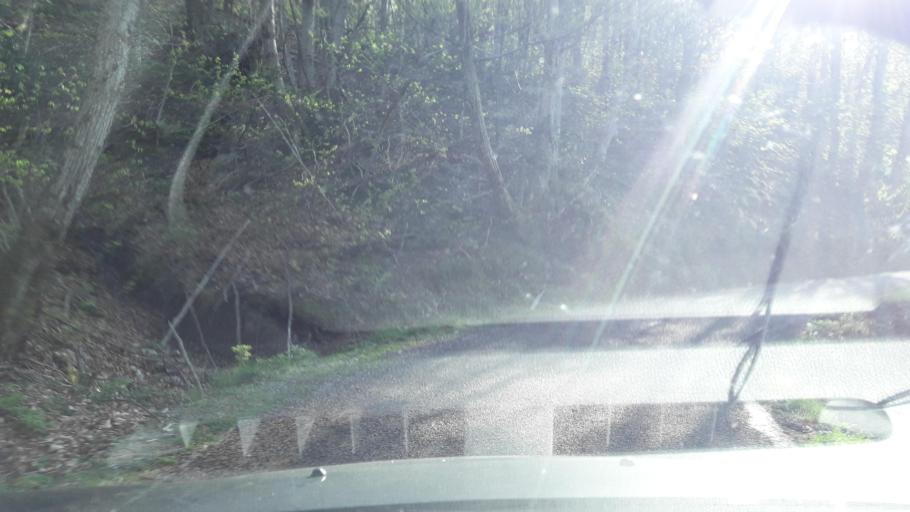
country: FR
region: Languedoc-Roussillon
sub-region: Departement du Gard
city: Valleraugue
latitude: 44.1036
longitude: 3.6653
